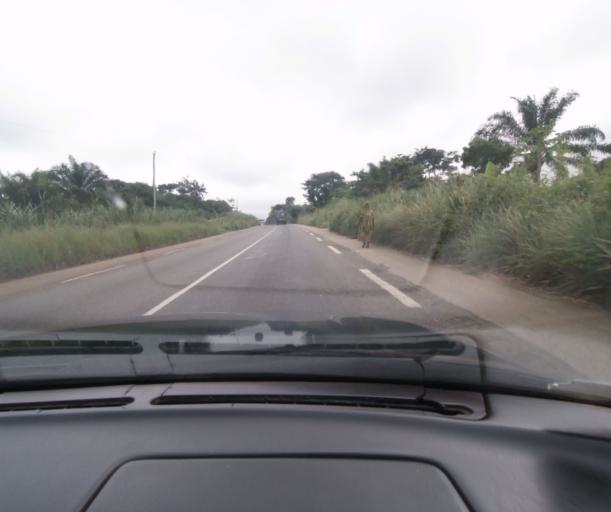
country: CM
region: Centre
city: Ombesa
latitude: 4.5705
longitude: 11.2661
